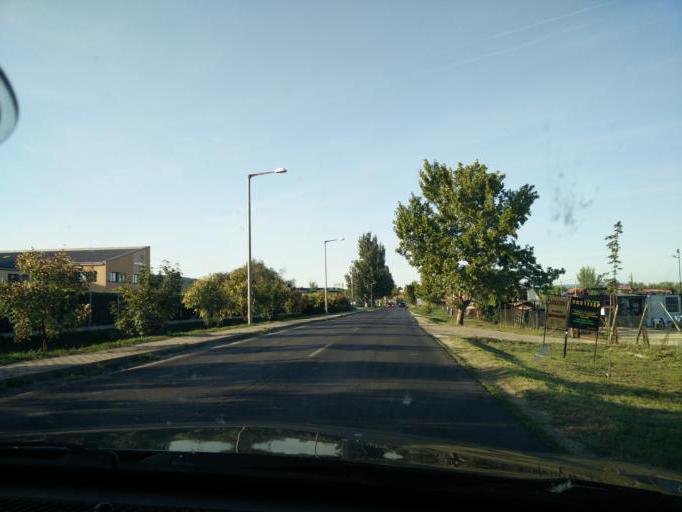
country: HU
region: Pest
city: Zsambek
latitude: 47.5393
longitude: 18.7233
